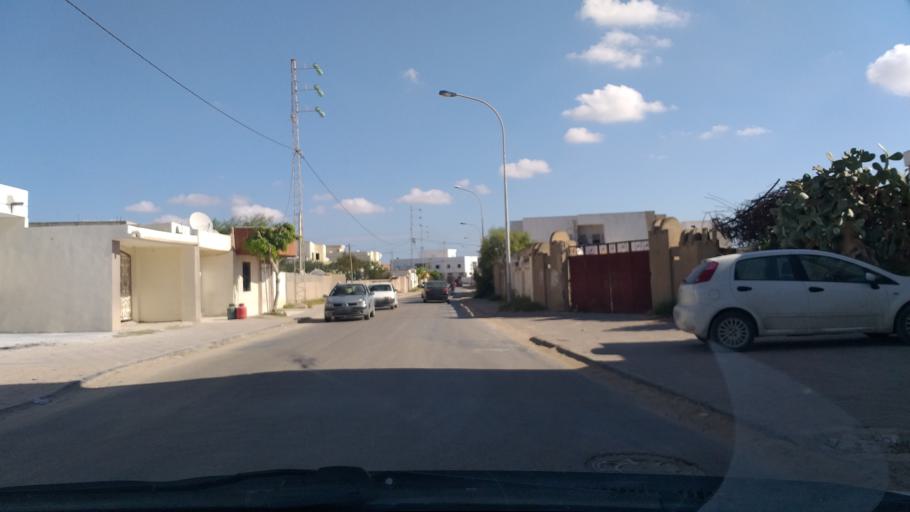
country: TN
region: Safaqis
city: Al Qarmadah
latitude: 34.8033
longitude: 10.7791
